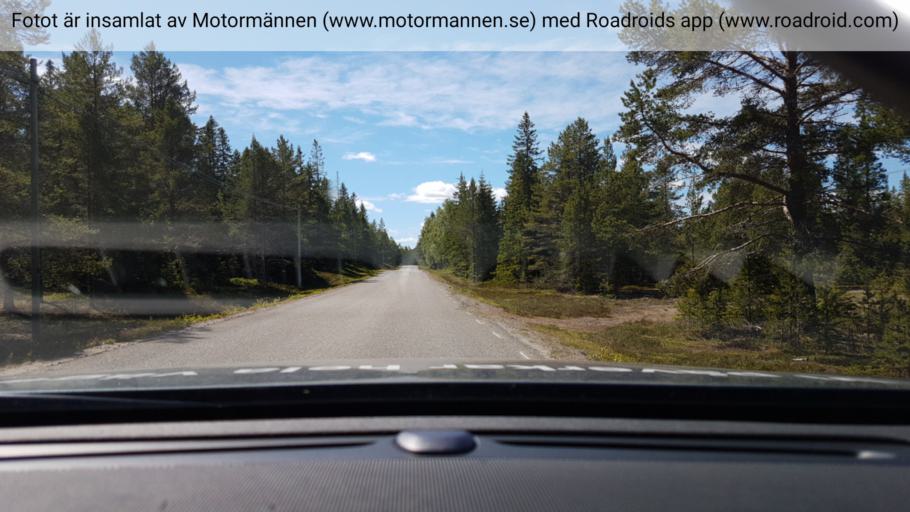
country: SE
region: Vaesterbotten
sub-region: Skelleftea Kommun
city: Burea
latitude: 64.4604
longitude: 21.5843
